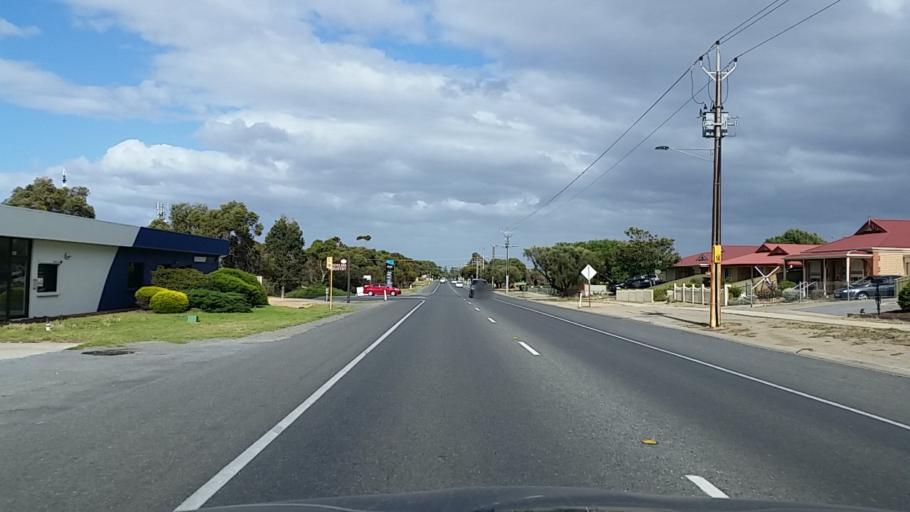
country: AU
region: South Australia
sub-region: Alexandrina
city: Goolwa
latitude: -35.5053
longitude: 138.7696
